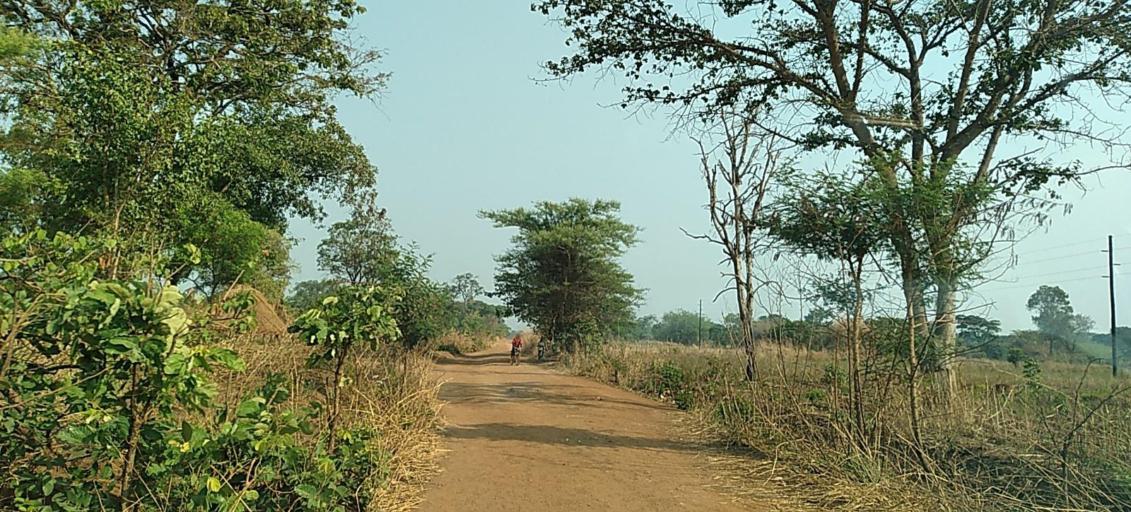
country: ZM
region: Copperbelt
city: Chingola
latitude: -12.8520
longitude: 27.5522
